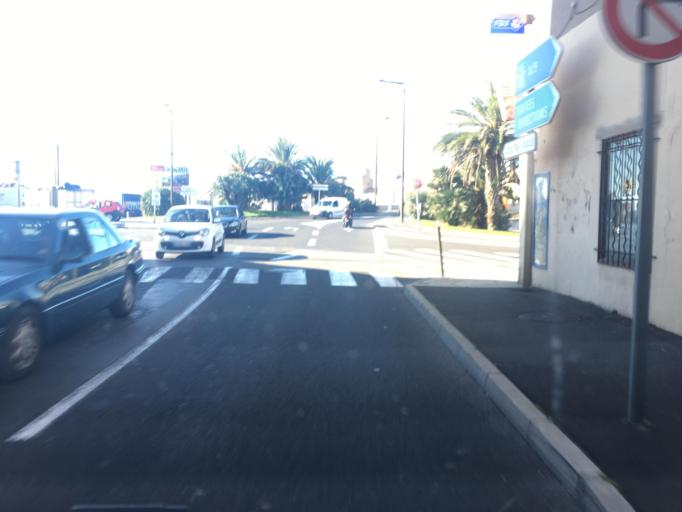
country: FR
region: Languedoc-Roussillon
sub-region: Departement de l'Herault
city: Sete
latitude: 43.4053
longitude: 3.7025
